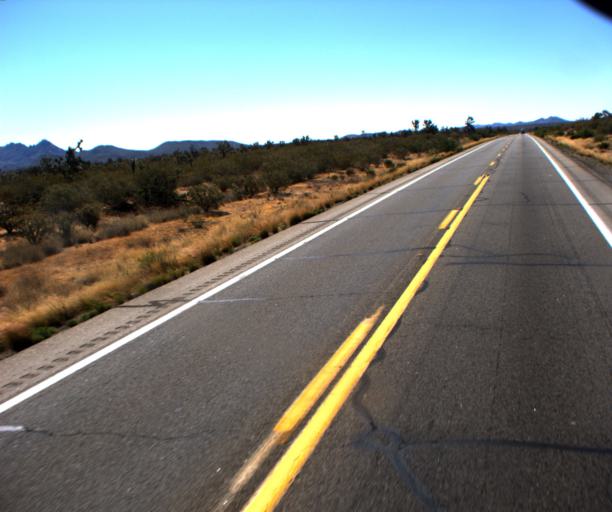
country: US
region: Arizona
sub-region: Yavapai County
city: Congress
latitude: 34.2397
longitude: -113.0757
